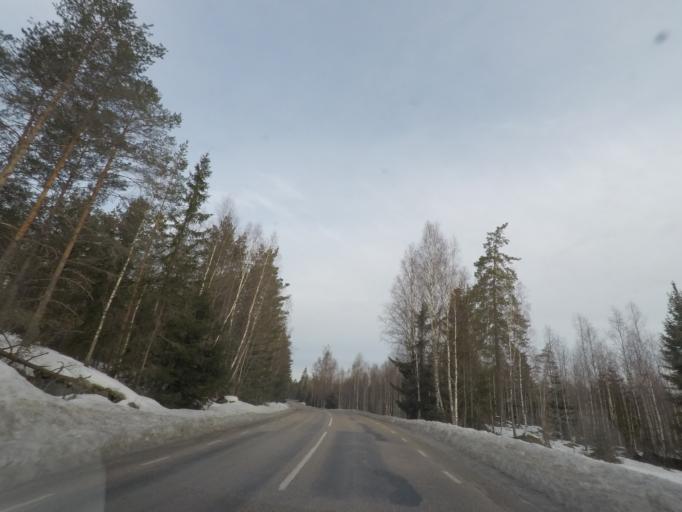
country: SE
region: Vaestmanland
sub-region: Surahammars Kommun
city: Surahammar
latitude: 59.7601
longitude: 16.2992
